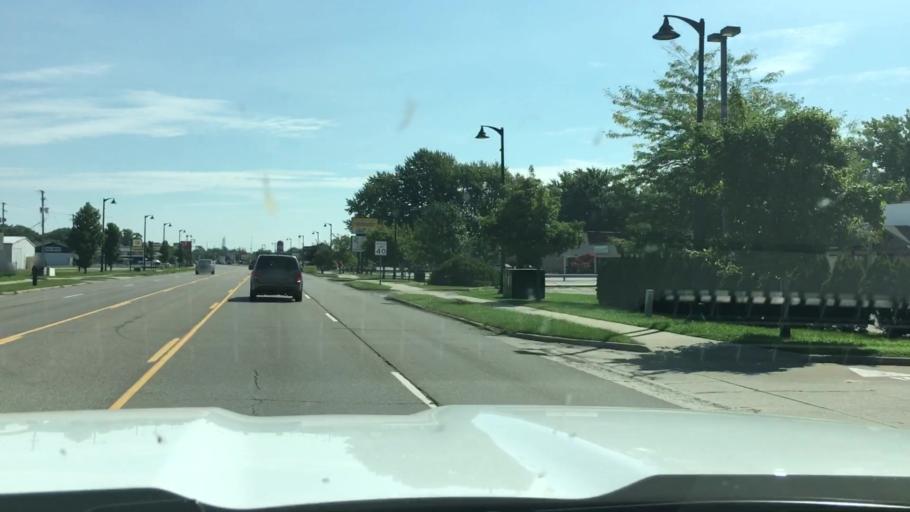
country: US
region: Michigan
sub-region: Bay County
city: Essexville
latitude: 43.5945
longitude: -83.8431
